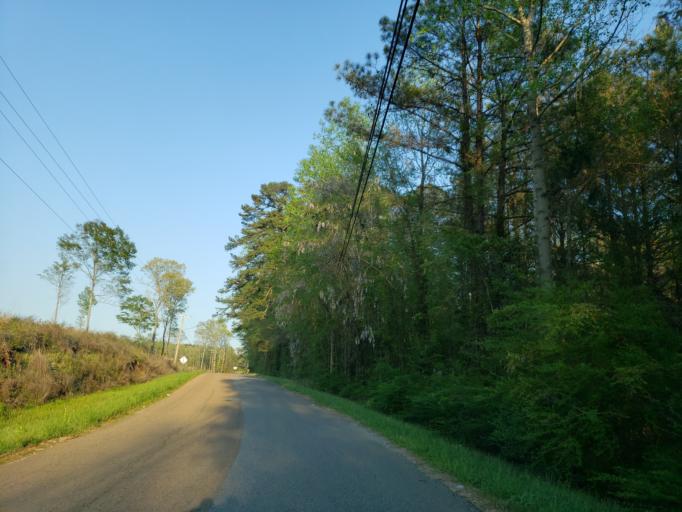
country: US
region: Mississippi
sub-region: Lauderdale County
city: Marion
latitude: 32.3989
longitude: -88.5888
